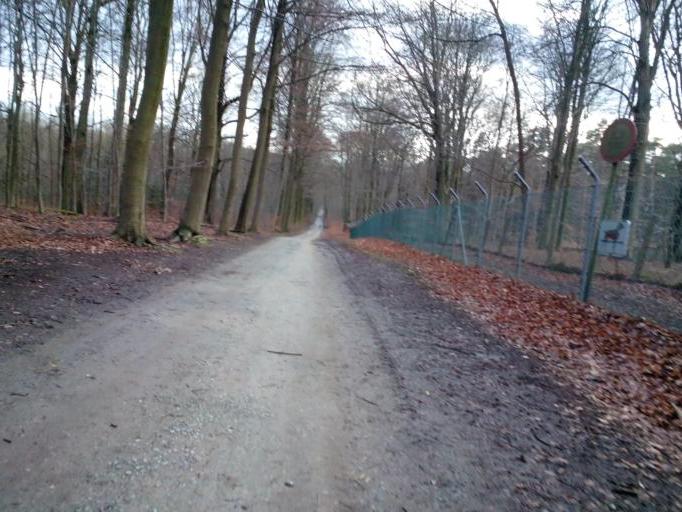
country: BE
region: Flanders
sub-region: Provincie Vlaams-Brabant
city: Oud-Heverlee
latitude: 50.8128
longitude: 4.6963
